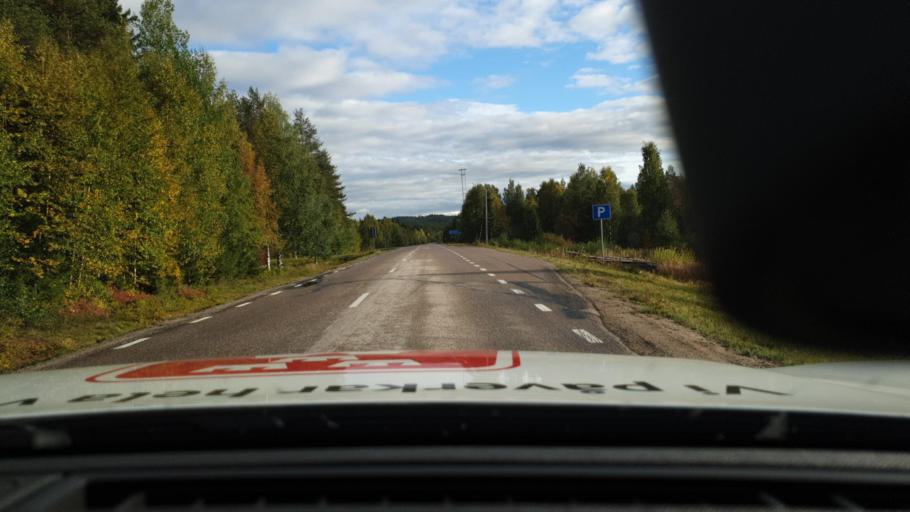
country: SE
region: Norrbotten
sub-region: Overkalix Kommun
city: OEverkalix
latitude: 66.6126
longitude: 22.7555
